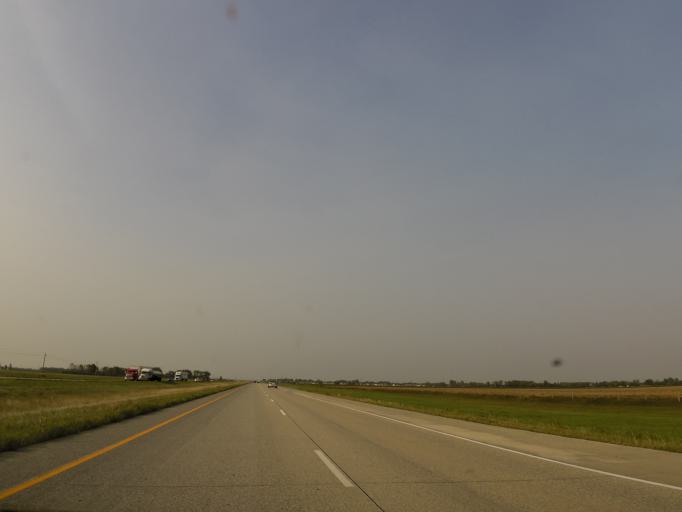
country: US
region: North Dakota
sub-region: Cass County
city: Horace
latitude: 46.7772
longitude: -96.8390
